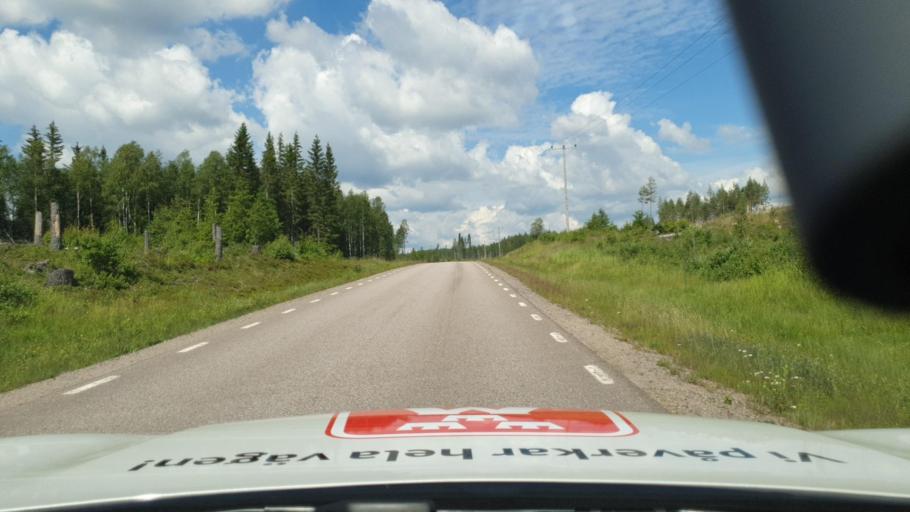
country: SE
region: Vaermland
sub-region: Torsby Kommun
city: Torsby
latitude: 60.4469
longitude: 12.8938
